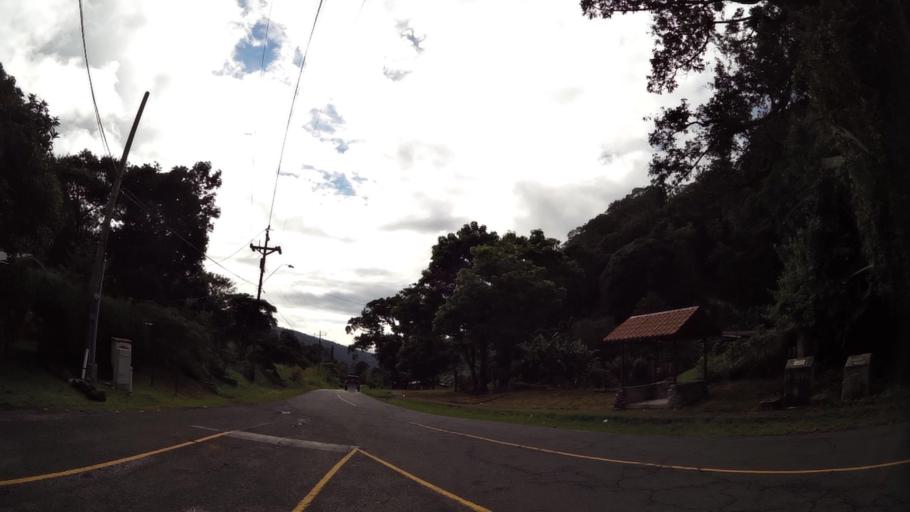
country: PA
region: Chiriqui
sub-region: Distrito Boquete
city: Boquete
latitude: 8.7987
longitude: -82.4514
